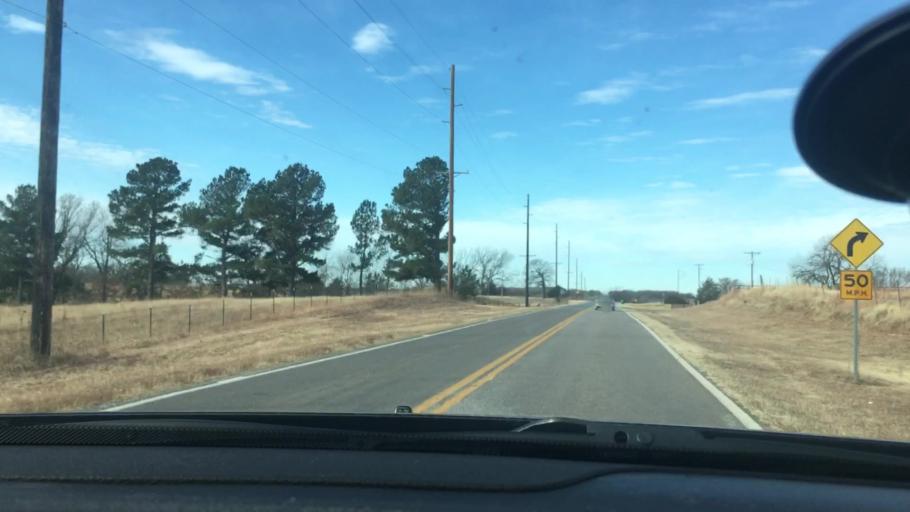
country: US
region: Oklahoma
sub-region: Seminole County
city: Konawa
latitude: 34.9417
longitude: -96.7084
